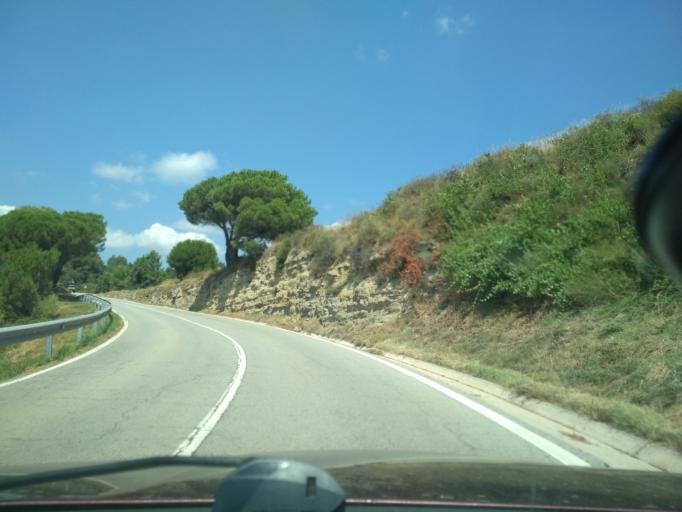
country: ES
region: Catalonia
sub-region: Provincia de Barcelona
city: Sant Feliu de Codines
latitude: 41.7018
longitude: 2.1662
